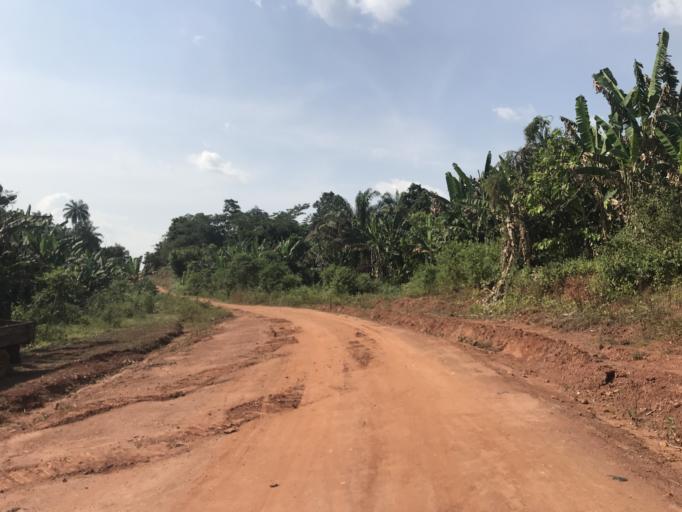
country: NG
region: Osun
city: Ilesa
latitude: 7.6348
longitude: 4.6751
